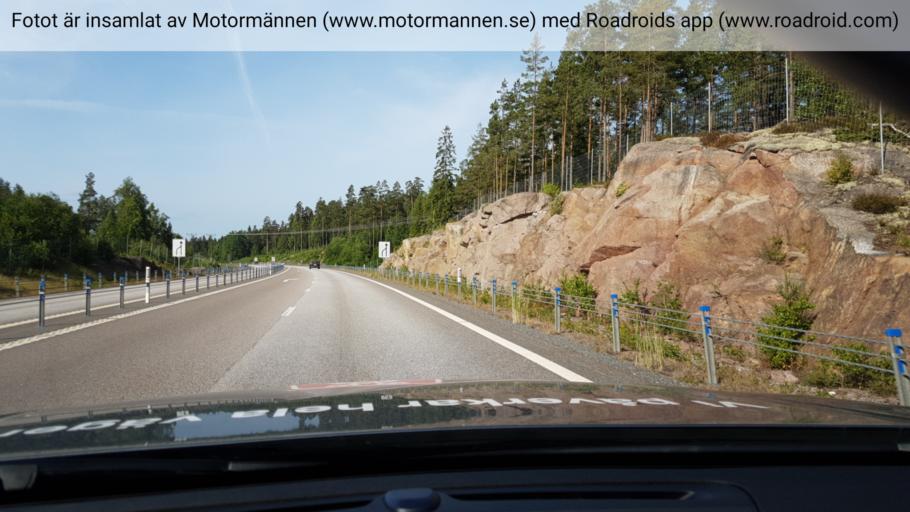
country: SE
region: OErebro
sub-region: Askersunds Kommun
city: Askersund
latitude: 58.7987
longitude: 14.8251
